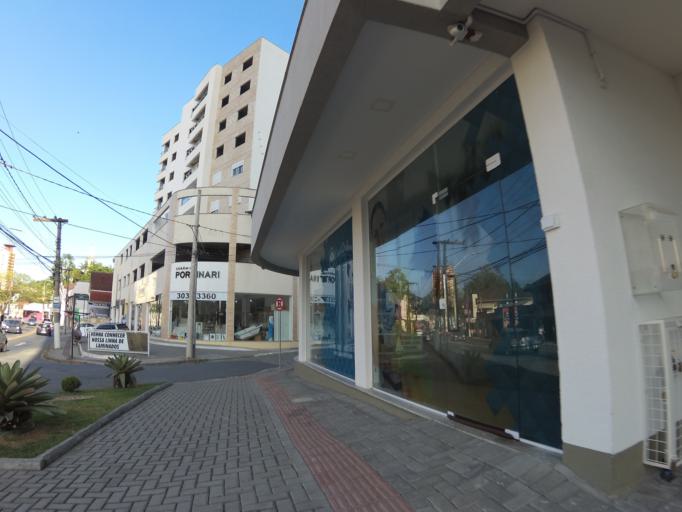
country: BR
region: Santa Catarina
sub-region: Blumenau
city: Blumenau
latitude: -26.9191
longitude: -49.0910
